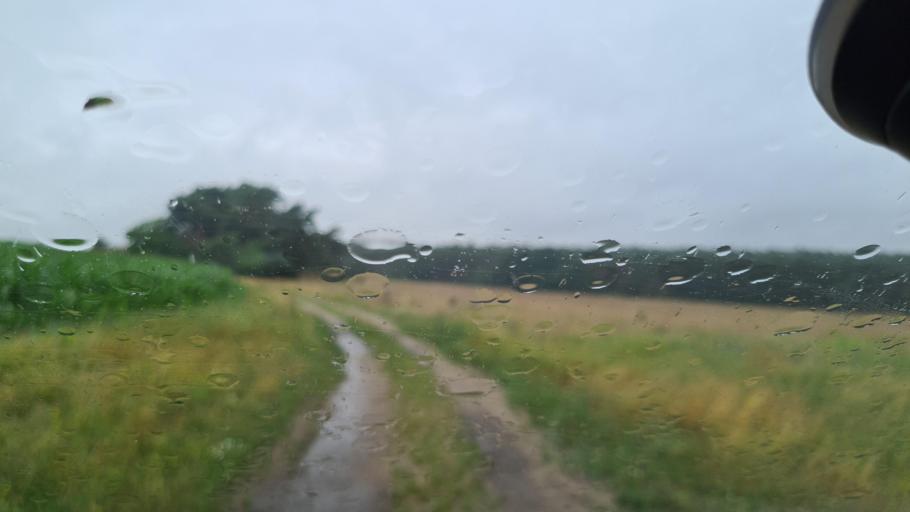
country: DE
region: Brandenburg
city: Juterbog
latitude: 51.9876
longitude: 13.1680
